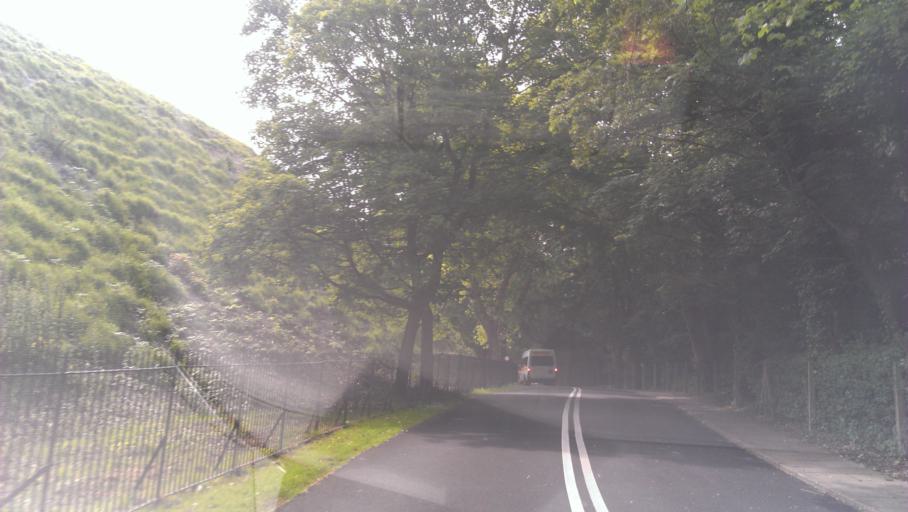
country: GB
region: England
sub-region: Kent
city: Dover
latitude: 51.1279
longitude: 1.3200
